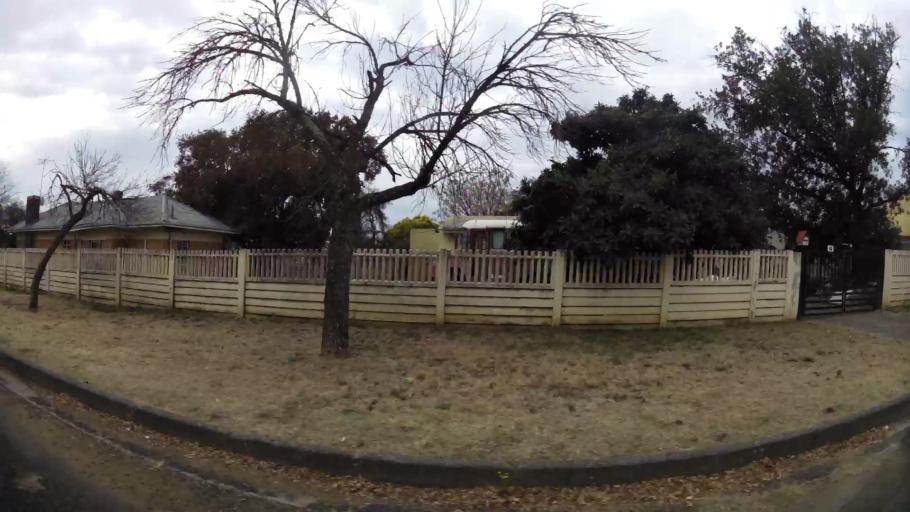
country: ZA
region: Orange Free State
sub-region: Fezile Dabi District Municipality
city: Kroonstad
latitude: -27.6841
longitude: 27.2350
